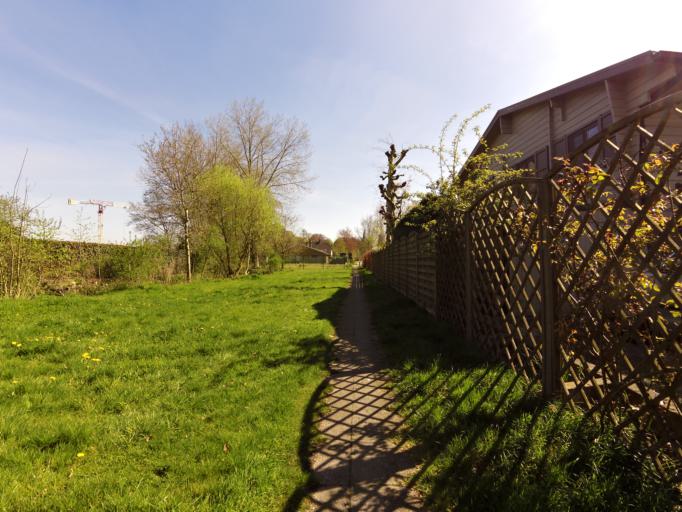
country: BE
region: Flanders
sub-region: Provincie West-Vlaanderen
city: Jabbeke
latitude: 51.1870
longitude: 3.0897
